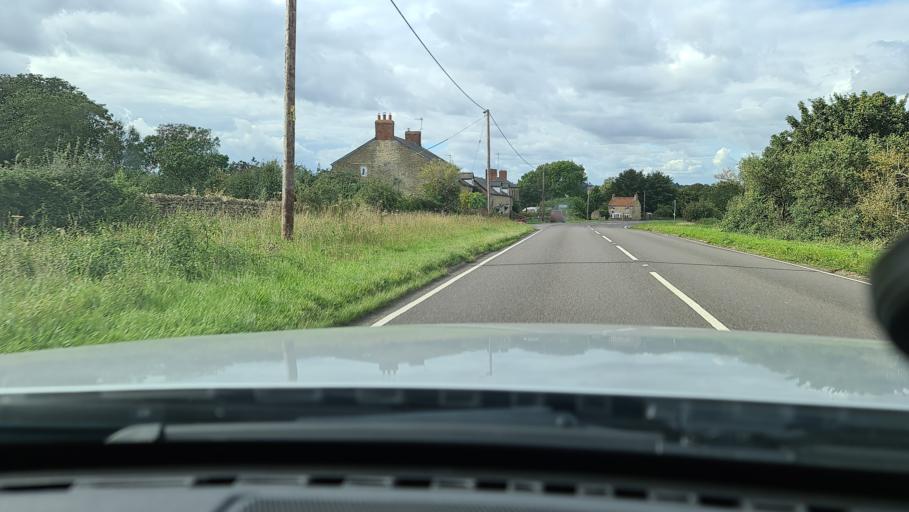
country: GB
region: England
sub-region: Oxfordshire
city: Somerton
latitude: 51.9760
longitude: -1.2338
